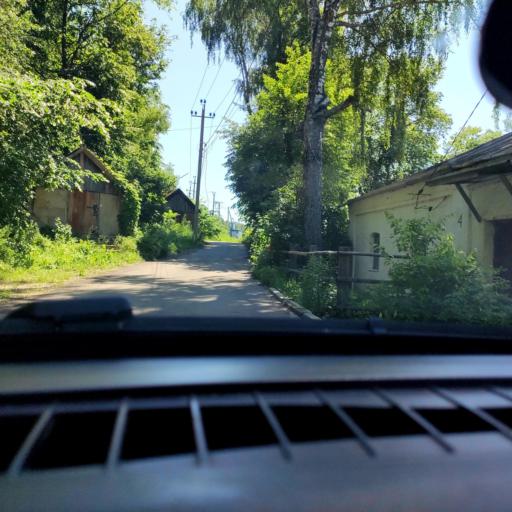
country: RU
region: Voronezj
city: Podgornoye
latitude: 51.7895
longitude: 39.1347
